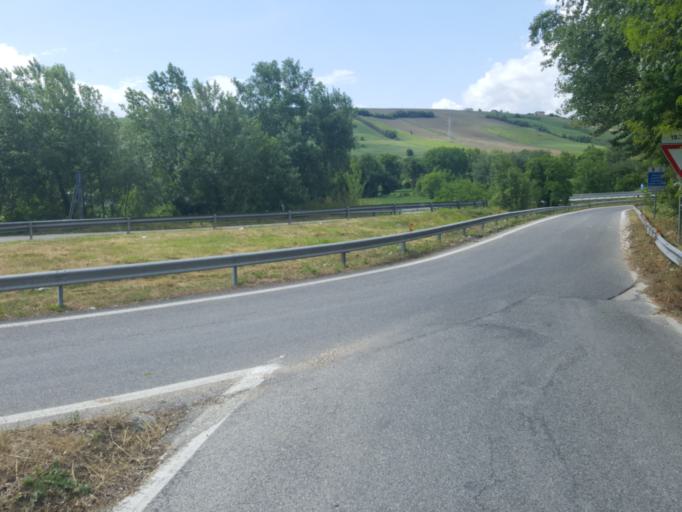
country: IT
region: The Marches
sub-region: Provincia di Macerata
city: Casette Verdini
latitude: 43.2351
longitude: 13.3686
